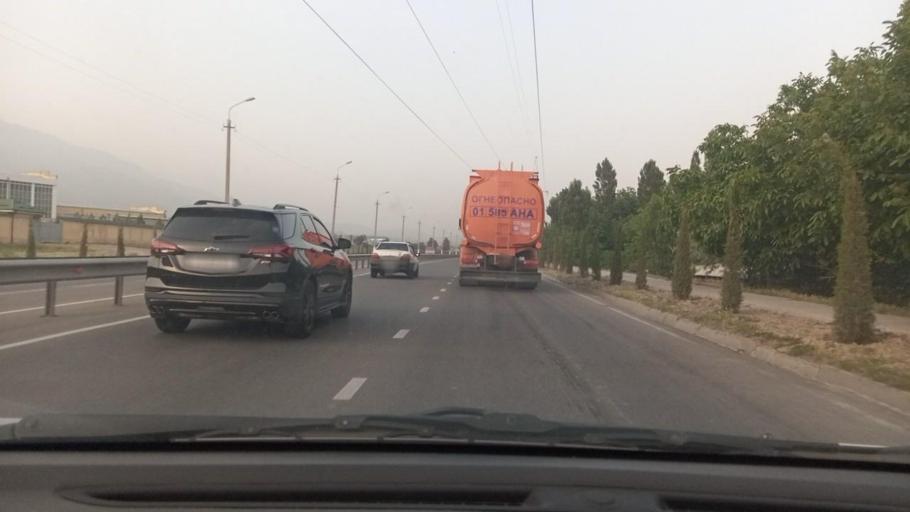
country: UZ
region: Toshkent
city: Angren
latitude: 41.0223
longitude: 70.1260
